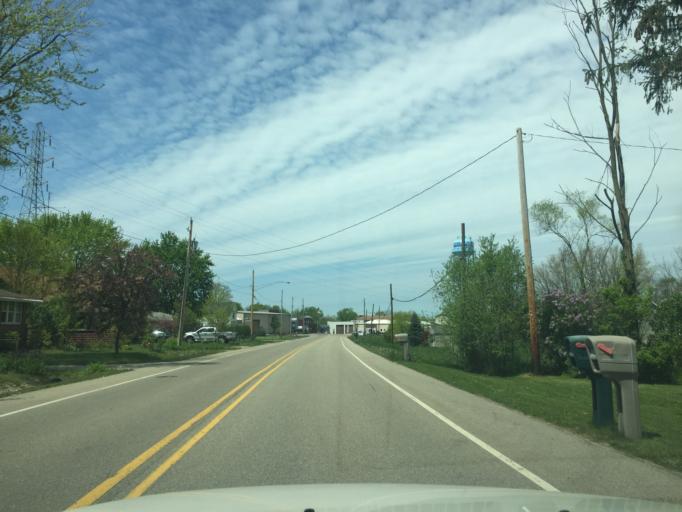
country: US
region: Michigan
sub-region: Berrien County
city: Stevensville
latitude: 41.9541
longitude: -86.4837
